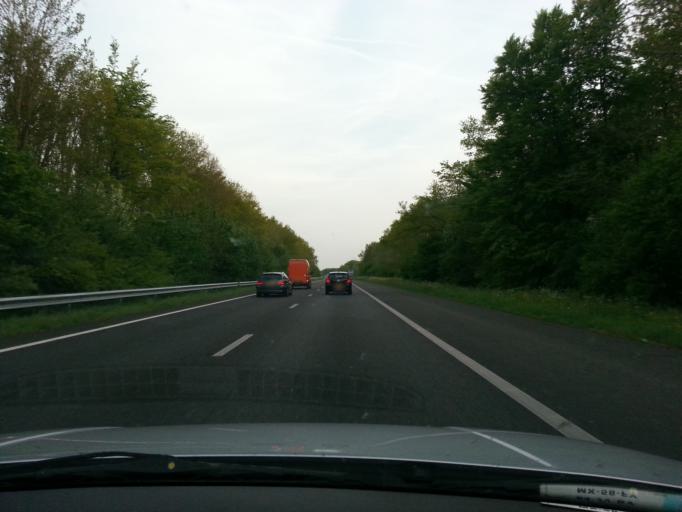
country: NL
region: Flevoland
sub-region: Gemeente Noordoostpolder
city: Emmeloord
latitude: 52.7420
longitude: 5.7685
